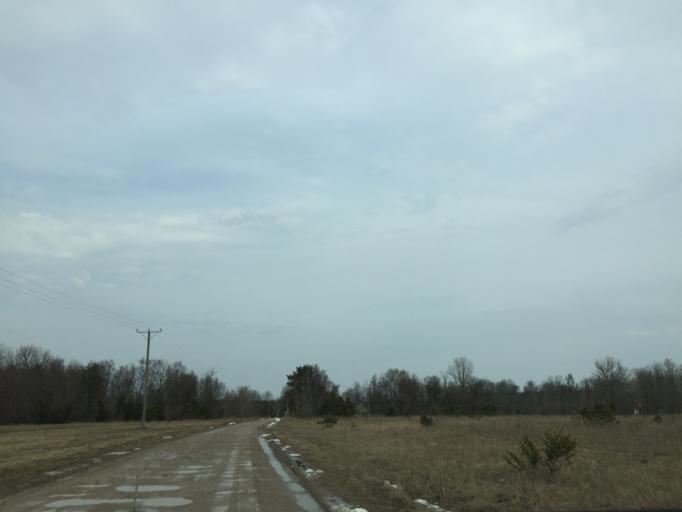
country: EE
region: Saare
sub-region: Kuressaare linn
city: Kuressaare
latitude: 58.4372
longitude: 22.1448
